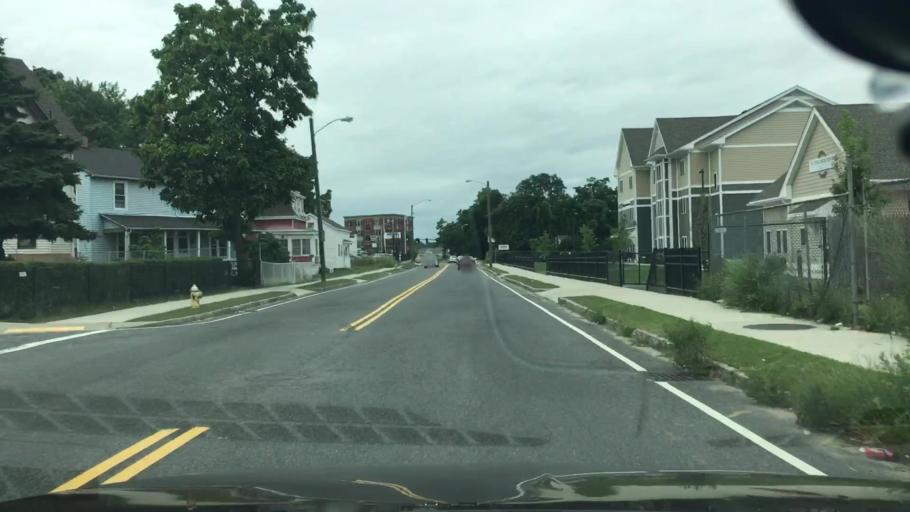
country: US
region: Massachusetts
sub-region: Hampden County
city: Springfield
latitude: 42.1118
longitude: -72.5765
